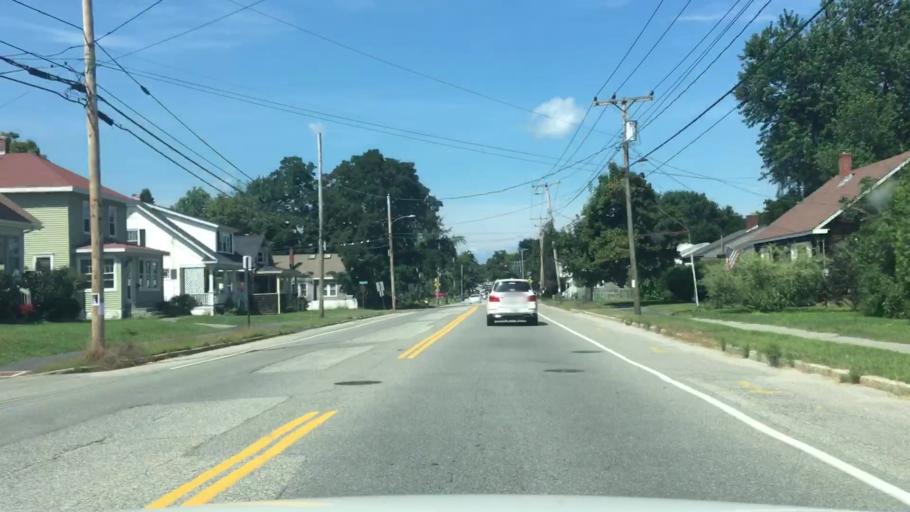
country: US
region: Maine
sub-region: Cumberland County
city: Portland
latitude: 43.6940
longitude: -70.2835
